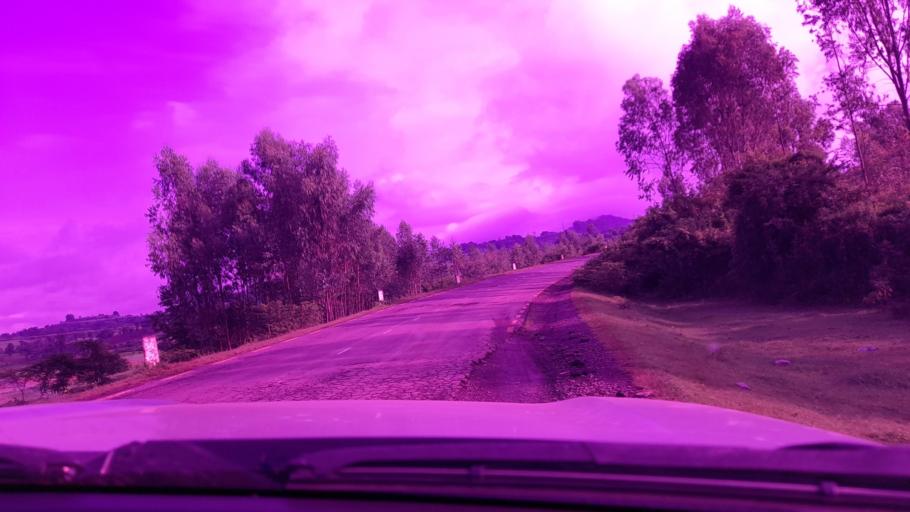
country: ET
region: Oromiya
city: Bedele
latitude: 8.2165
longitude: 36.4447
